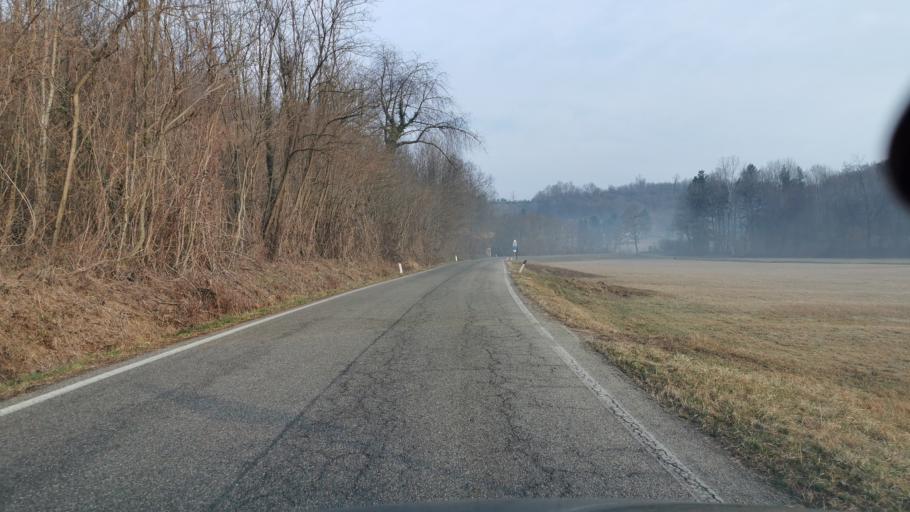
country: IT
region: Piedmont
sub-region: Provincia di Torino
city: Vialfre
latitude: 45.3730
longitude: 7.8222
